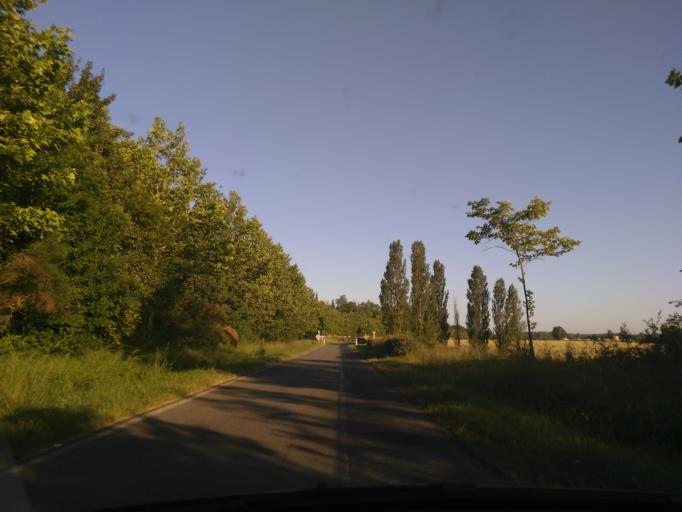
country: FR
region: Midi-Pyrenees
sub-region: Departement du Gers
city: Valence-sur-Baise
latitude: 43.8798
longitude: 0.3885
